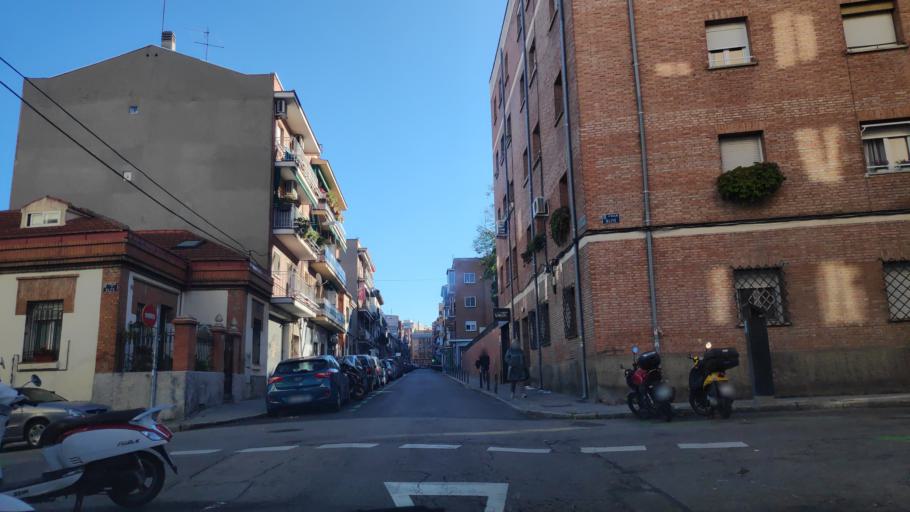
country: ES
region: Madrid
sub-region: Provincia de Madrid
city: Tetuan de las Victorias
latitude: 40.4517
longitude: -3.7071
